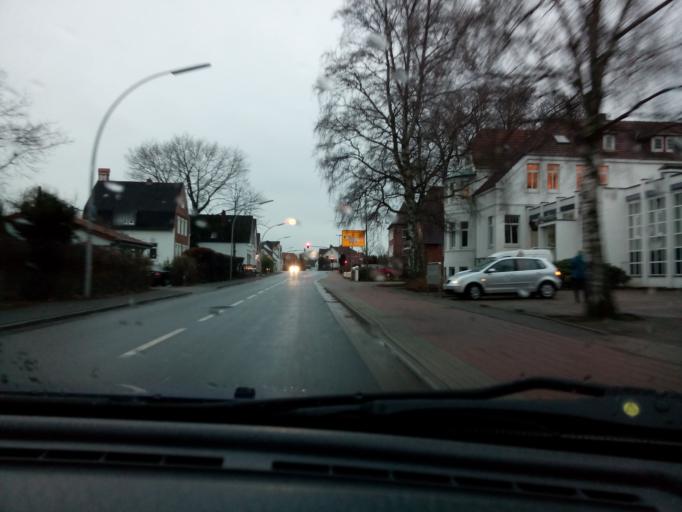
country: DE
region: Lower Saxony
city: Osterholz-Scharmbeck
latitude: 53.2221
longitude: 8.8037
